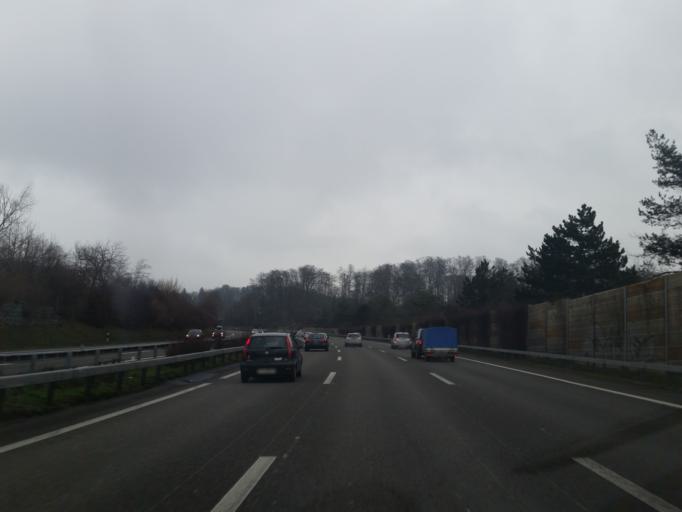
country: CH
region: Zurich
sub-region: Bezirk Pfaeffikon
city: Tagelswangen
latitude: 47.4236
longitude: 8.6725
